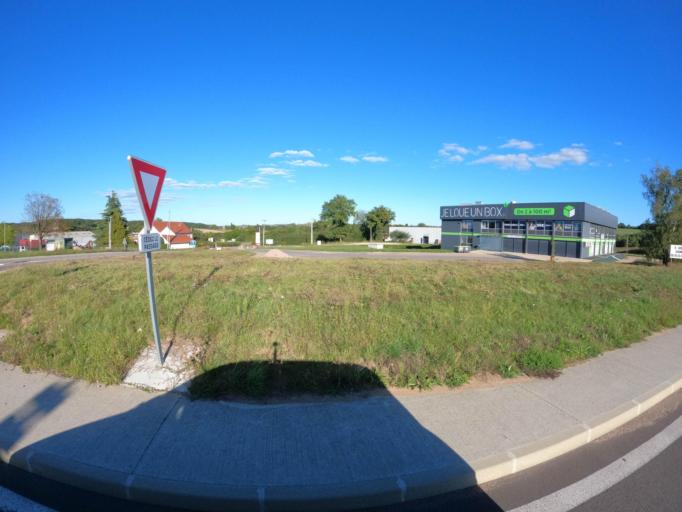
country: FR
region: Bourgogne
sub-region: Departement de Saone-et-Loire
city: Blanzy
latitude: 46.7034
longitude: 4.4108
